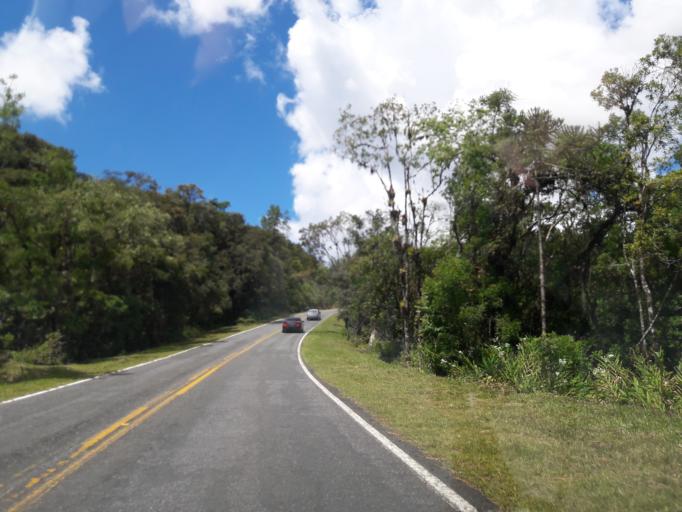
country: BR
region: Parana
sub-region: Campina Grande Do Sul
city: Campina Grande do Sul
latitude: -25.3230
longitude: -48.9225
